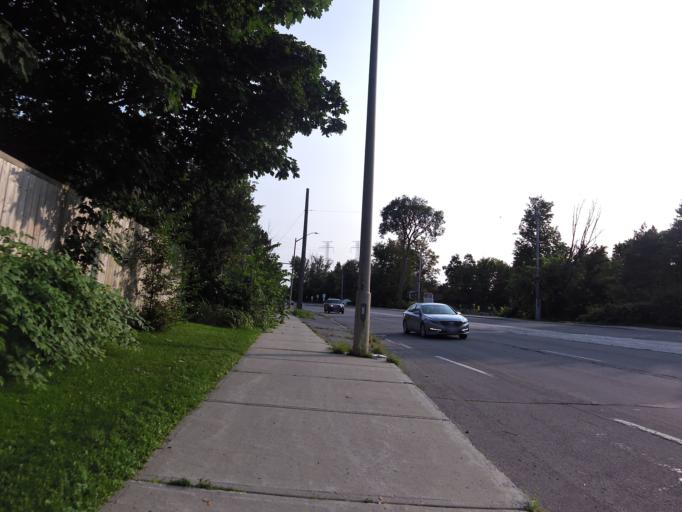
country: CA
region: Ontario
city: Ottawa
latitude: 45.3549
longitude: -75.6918
